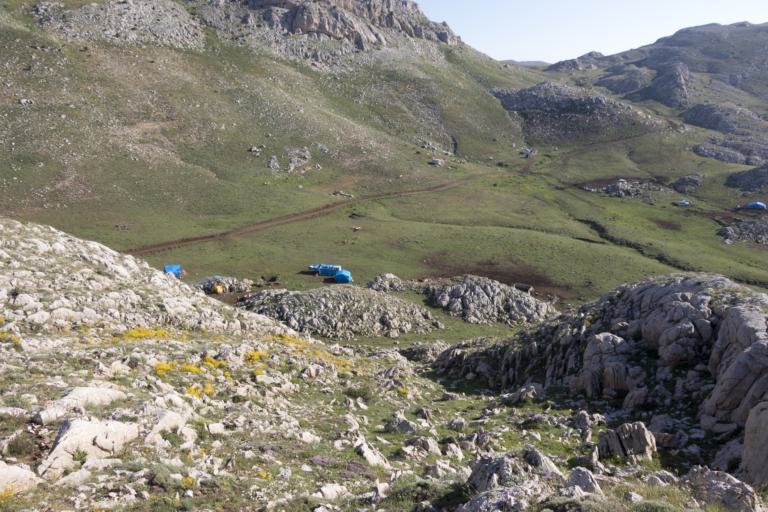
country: TR
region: Adana
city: Tufanbeyli
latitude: 38.3960
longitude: 36.1738
